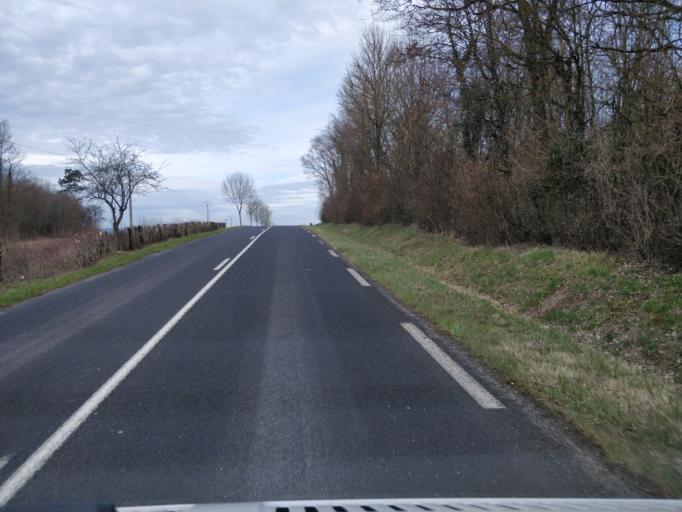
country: FR
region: Lorraine
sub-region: Departement de Meurthe-et-Moselle
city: Montauville
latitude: 48.9250
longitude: 5.9076
